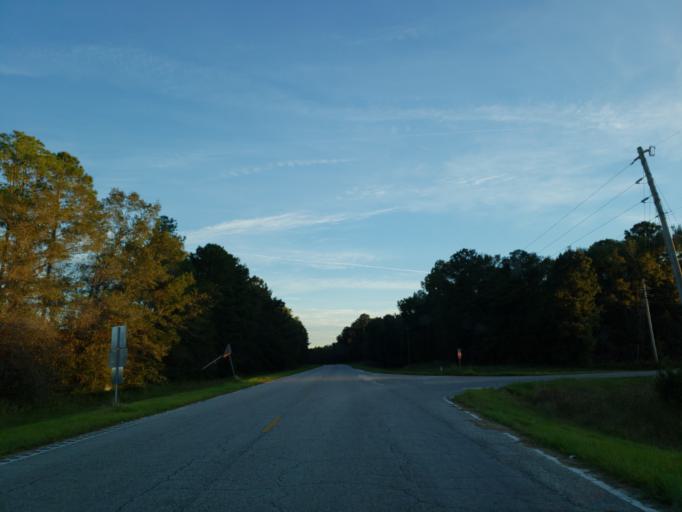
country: US
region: Mississippi
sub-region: Wayne County
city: Belmont
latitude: 31.4159
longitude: -88.4711
